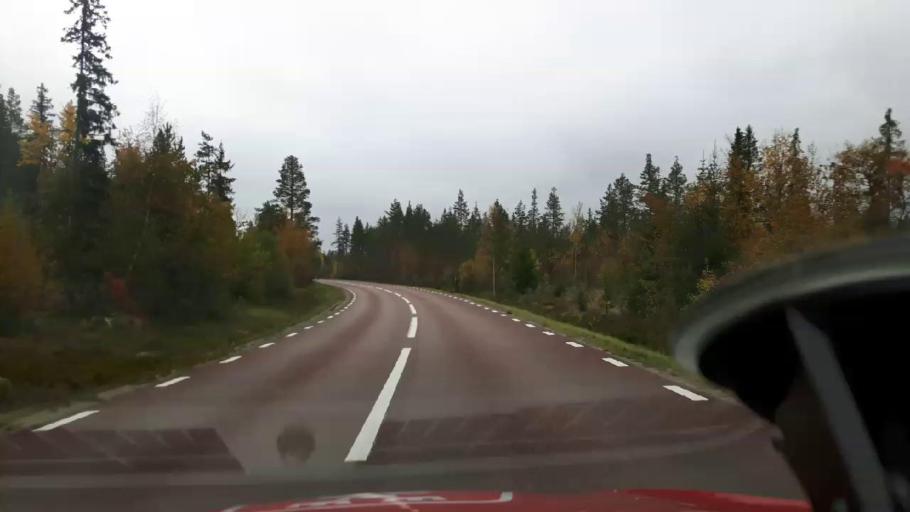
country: SE
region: Jaemtland
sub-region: Harjedalens Kommun
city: Sveg
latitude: 62.3169
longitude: 14.7476
